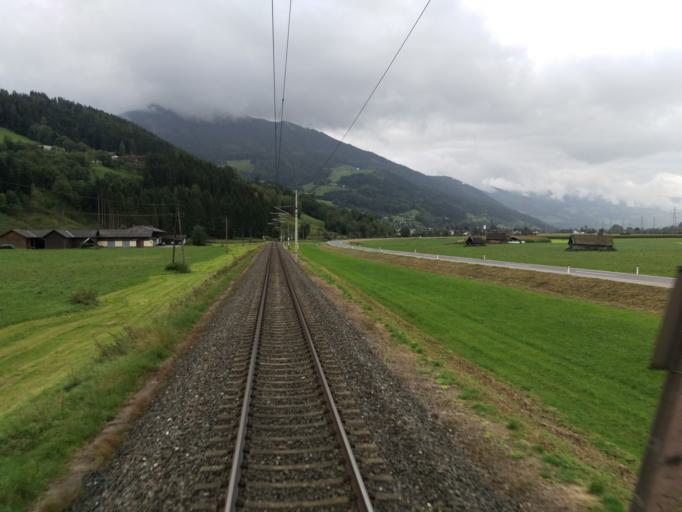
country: AT
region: Styria
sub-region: Politischer Bezirk Liezen
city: Niederoblarn
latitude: 47.4725
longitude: 14.0084
